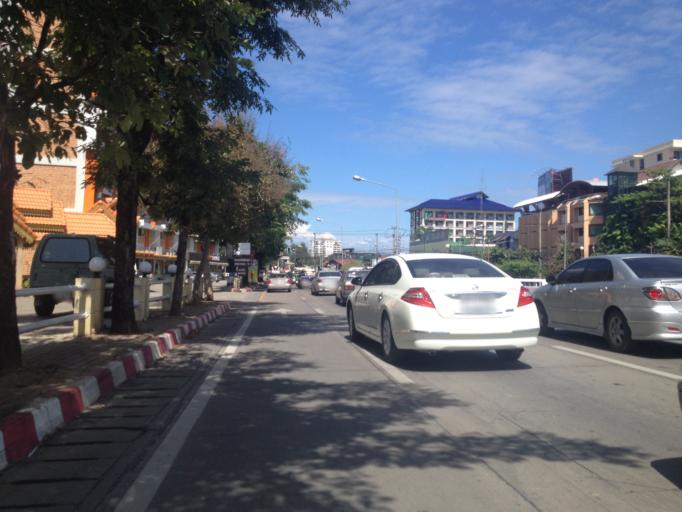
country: TH
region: Chiang Mai
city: Chiang Mai
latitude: 18.8044
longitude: 98.9594
